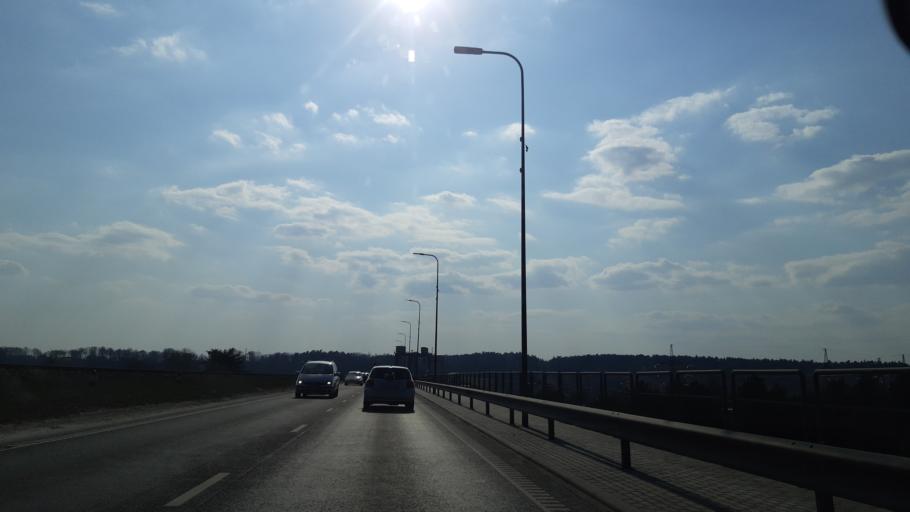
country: LT
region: Kauno apskritis
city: Dainava (Kaunas)
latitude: 54.8770
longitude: 24.0064
